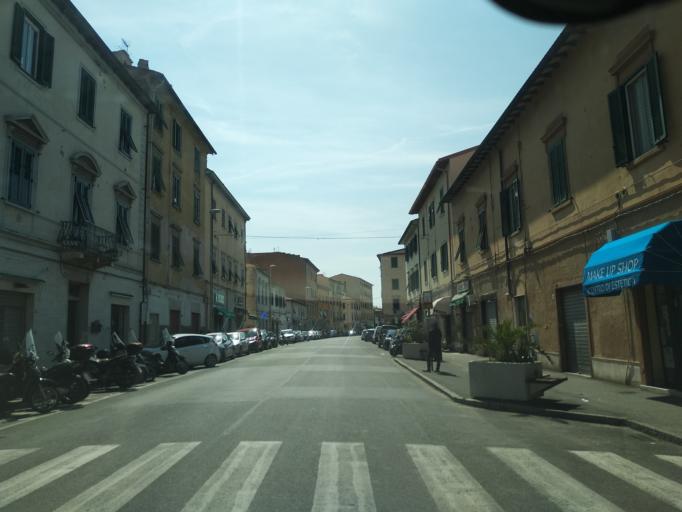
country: IT
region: Tuscany
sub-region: Provincia di Livorno
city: Livorno
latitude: 43.5613
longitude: 10.3282
